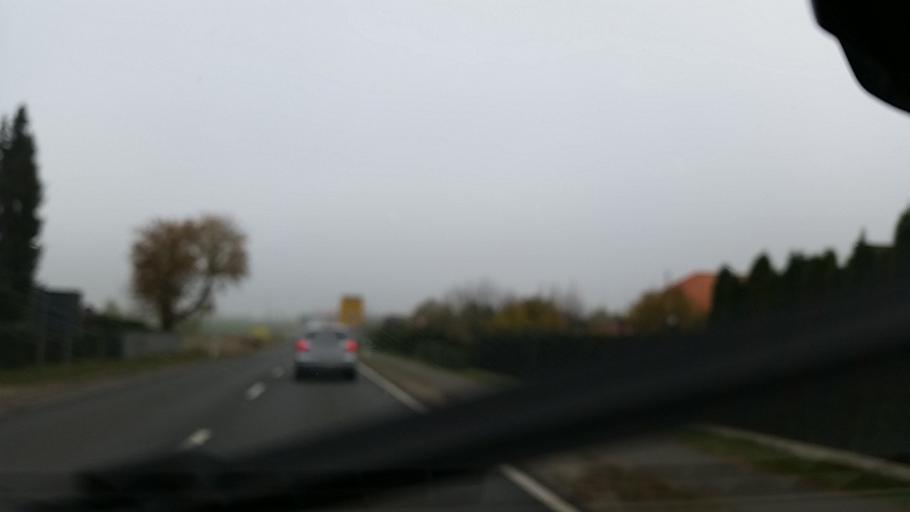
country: DE
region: Lower Saxony
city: Danndorf
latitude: 52.4277
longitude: 10.8477
